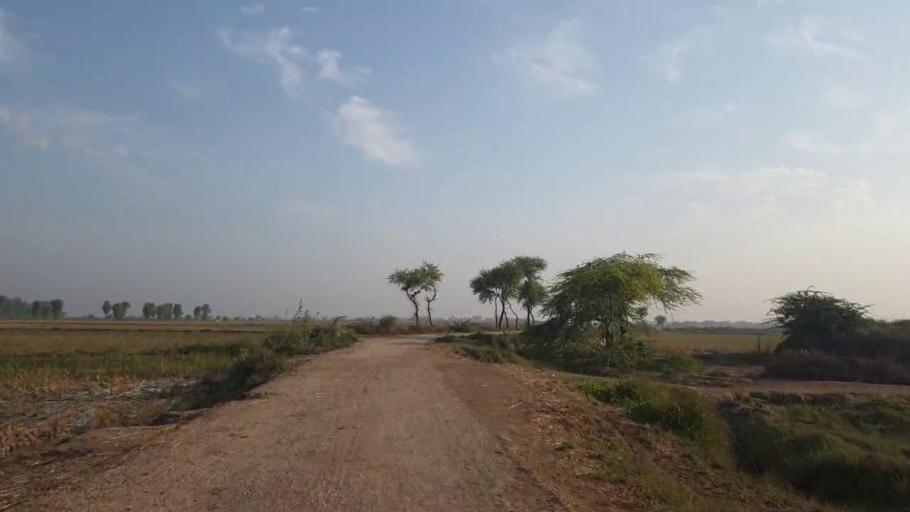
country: PK
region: Sindh
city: Tando Bago
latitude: 24.8204
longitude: 68.9578
